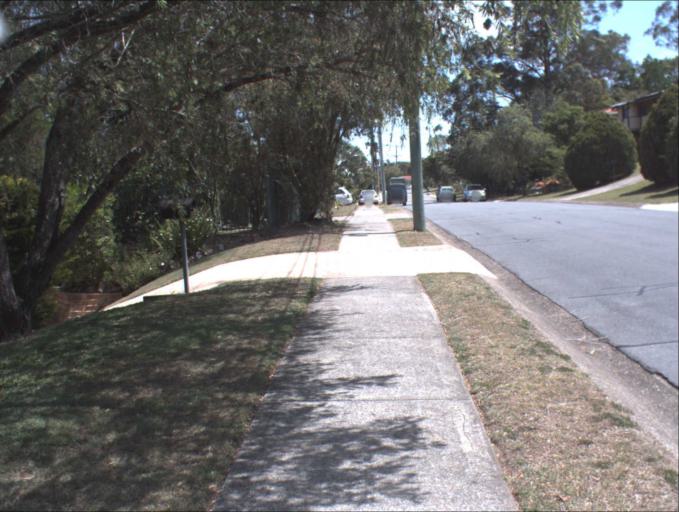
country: AU
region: Queensland
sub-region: Logan
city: Rochedale South
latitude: -27.5968
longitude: 153.1448
